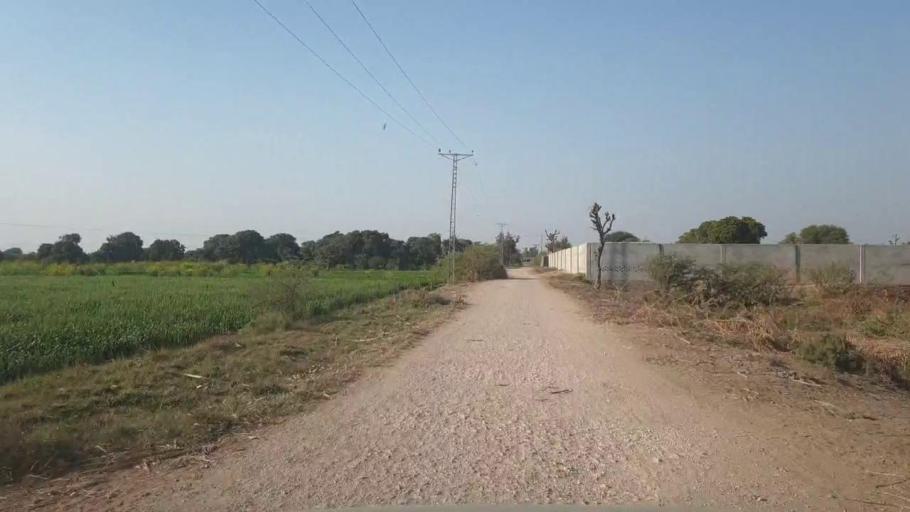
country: PK
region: Sindh
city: Chambar
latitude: 25.3003
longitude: 68.8728
